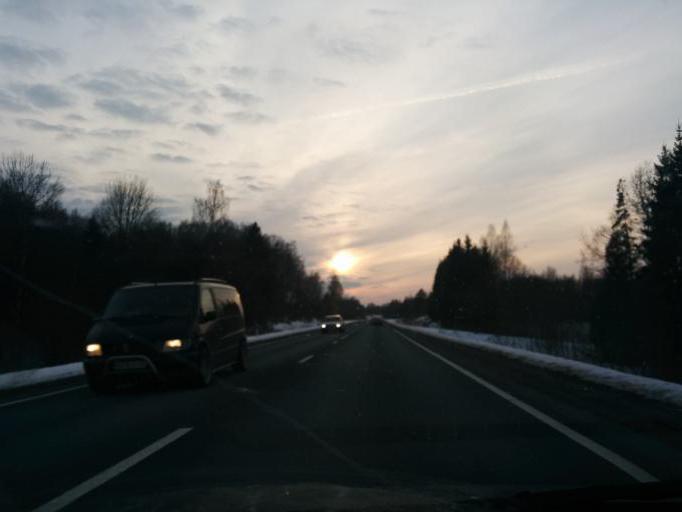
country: LV
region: Raunas
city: Rauna
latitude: 57.2986
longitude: 25.5831
